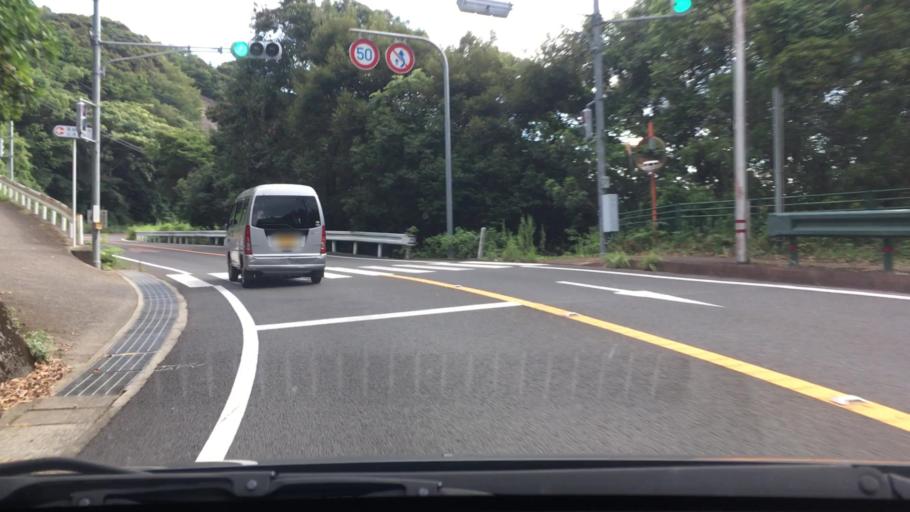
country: JP
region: Nagasaki
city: Togitsu
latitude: 32.8397
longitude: 129.7056
